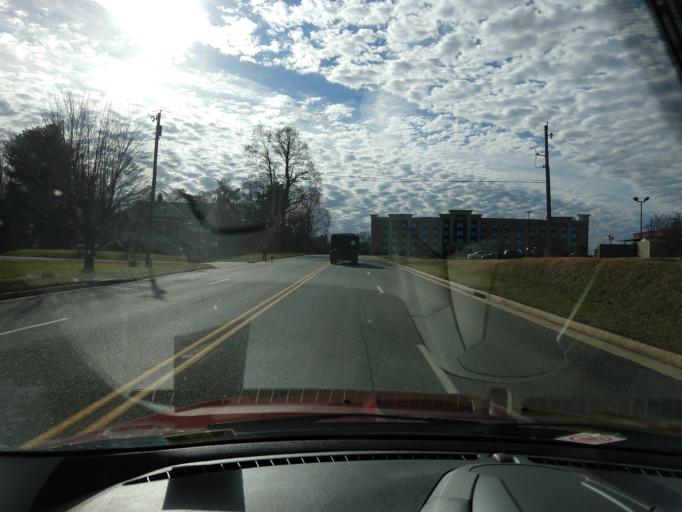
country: US
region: Virginia
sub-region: City of Lynchburg
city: West Lynchburg
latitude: 37.3353
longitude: -79.1900
